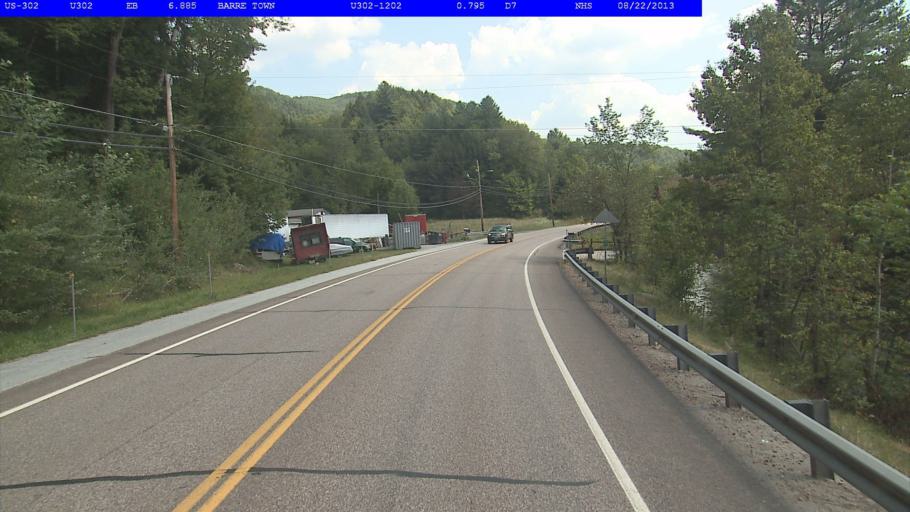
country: US
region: Vermont
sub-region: Washington County
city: South Barre
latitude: 44.1789
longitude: -72.4713
